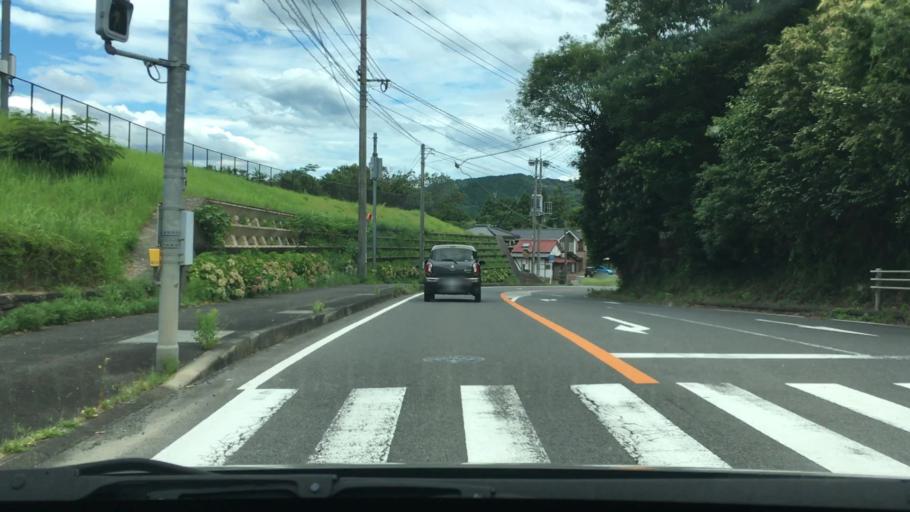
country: JP
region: Nagasaki
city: Sasebo
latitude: 32.9930
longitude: 129.7360
